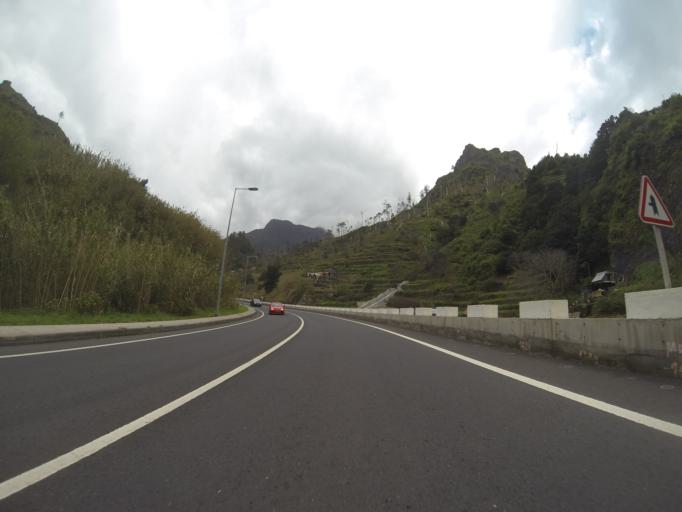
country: PT
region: Madeira
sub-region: Camara de Lobos
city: Curral das Freiras
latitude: 32.7302
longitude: -17.0211
